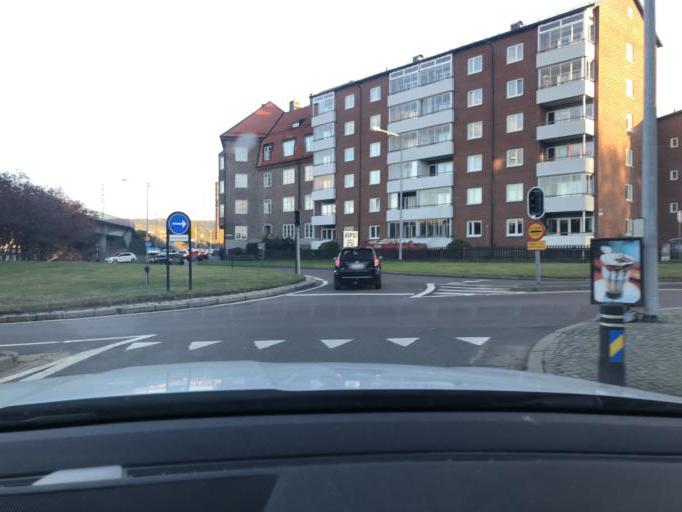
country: SE
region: Joenkoeping
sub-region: Jonkopings Kommun
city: Jonkoping
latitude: 57.7818
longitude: 14.1886
